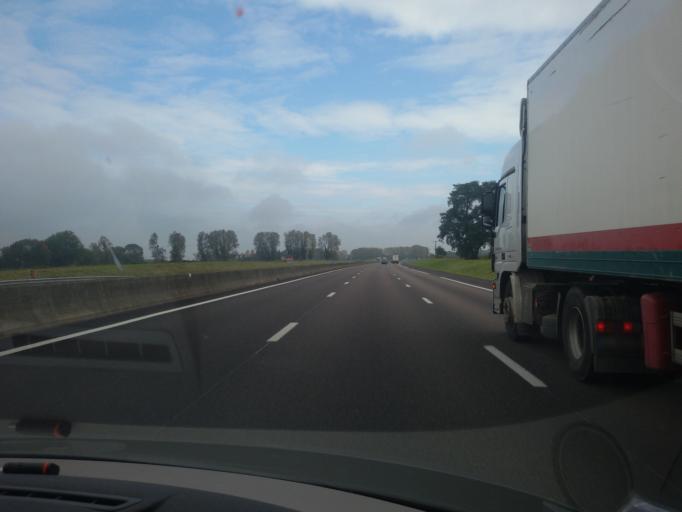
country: FR
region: Haute-Normandie
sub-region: Departement de l'Eure
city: Hauville
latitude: 49.3699
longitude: 0.7631
